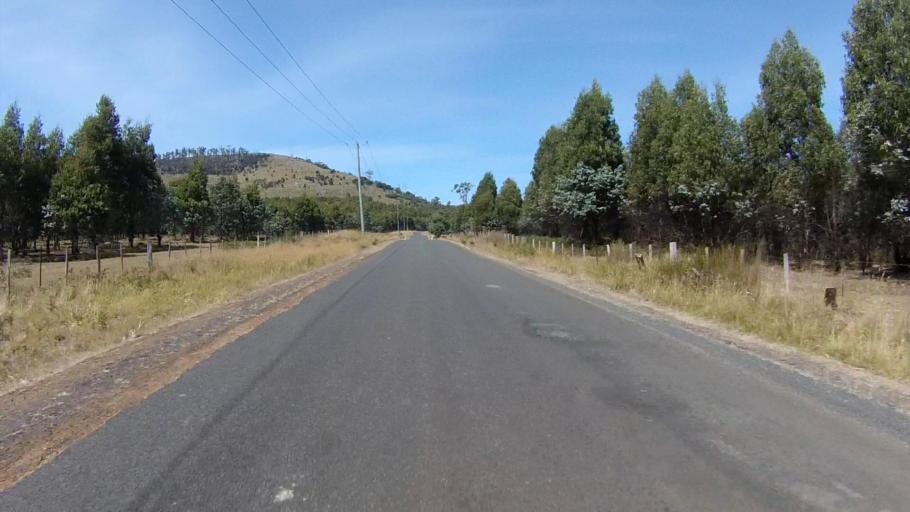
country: AU
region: Tasmania
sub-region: Sorell
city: Sorell
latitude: -42.6214
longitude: 147.7296
